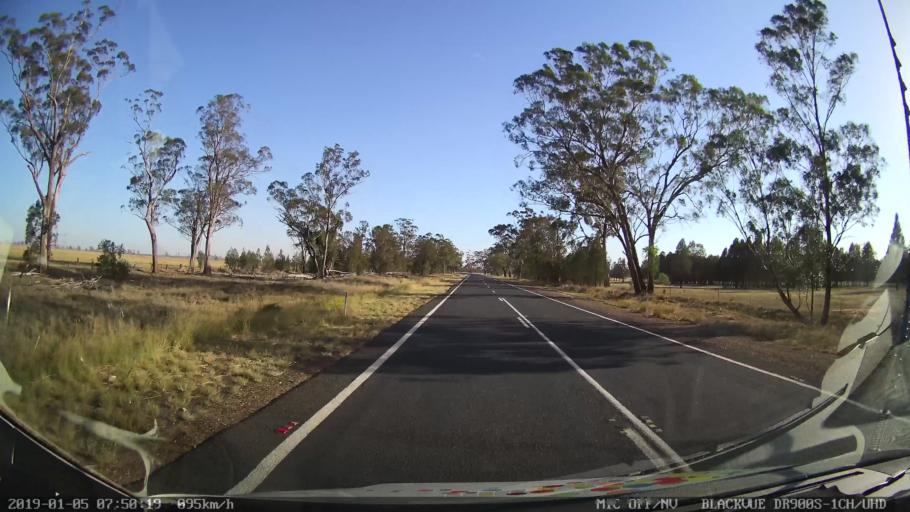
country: AU
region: New South Wales
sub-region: Gilgandra
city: Gilgandra
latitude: -31.7891
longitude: 148.6362
